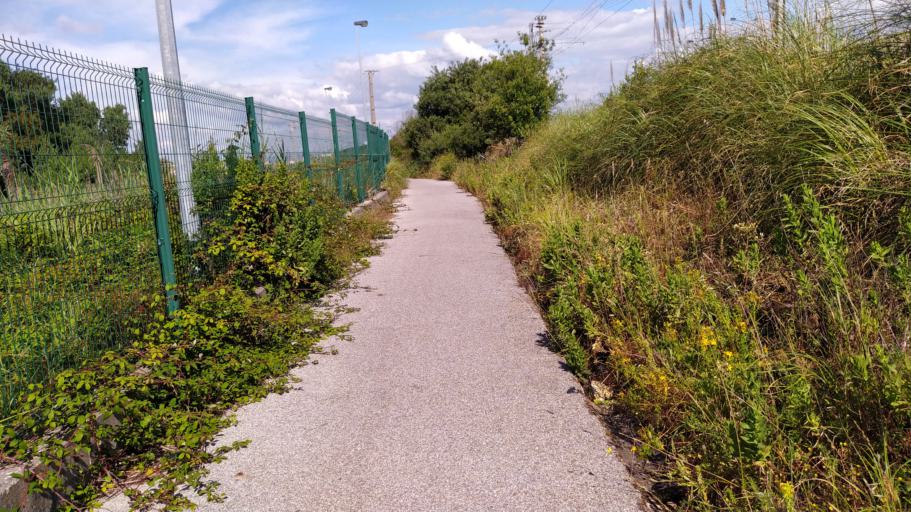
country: PT
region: Aveiro
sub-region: Ilhavo
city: Gafanha da Nazare
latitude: 40.6330
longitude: -8.6850
